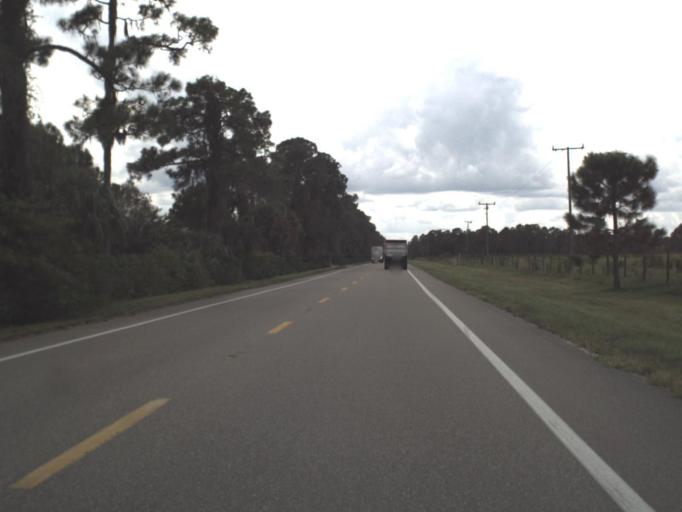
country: US
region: Florida
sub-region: DeSoto County
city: Nocatee
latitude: 26.9800
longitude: -81.7606
